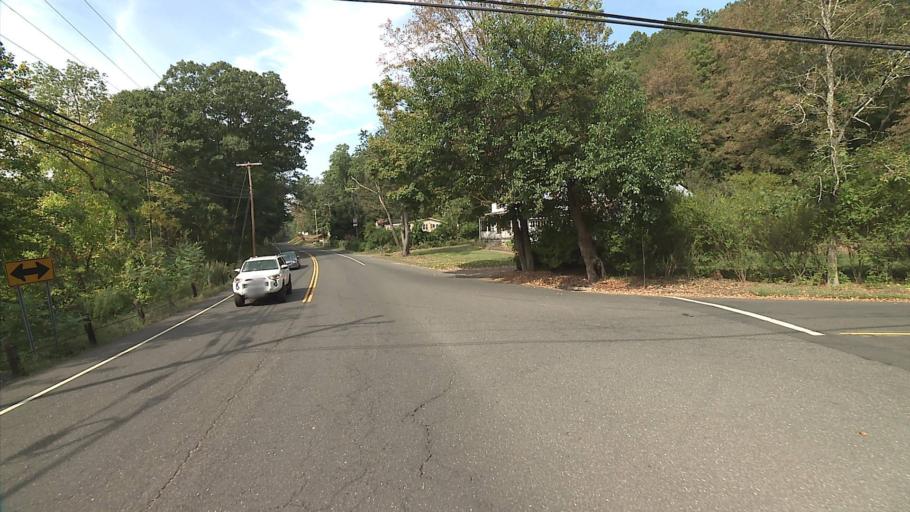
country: US
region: Connecticut
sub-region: New Haven County
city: Oxford
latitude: 41.3843
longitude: -73.1602
